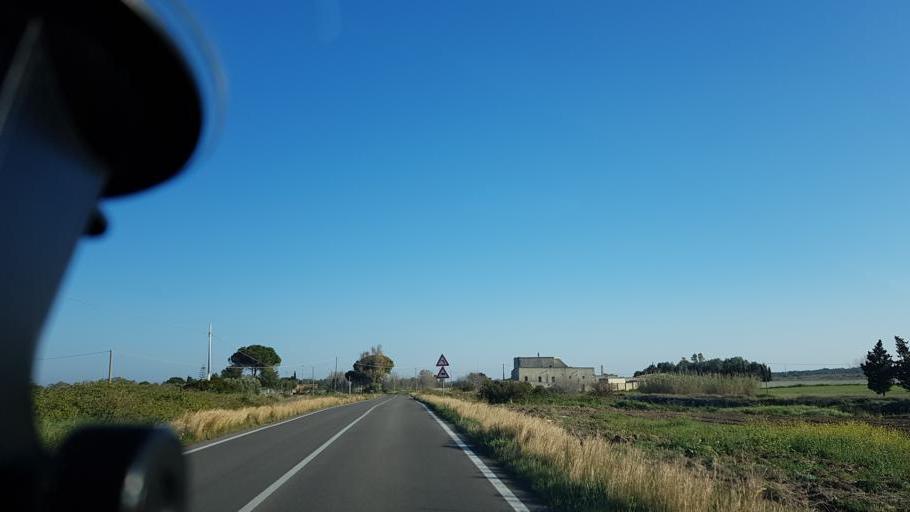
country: IT
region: Apulia
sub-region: Provincia di Lecce
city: Merine
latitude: 40.4142
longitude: 18.2533
